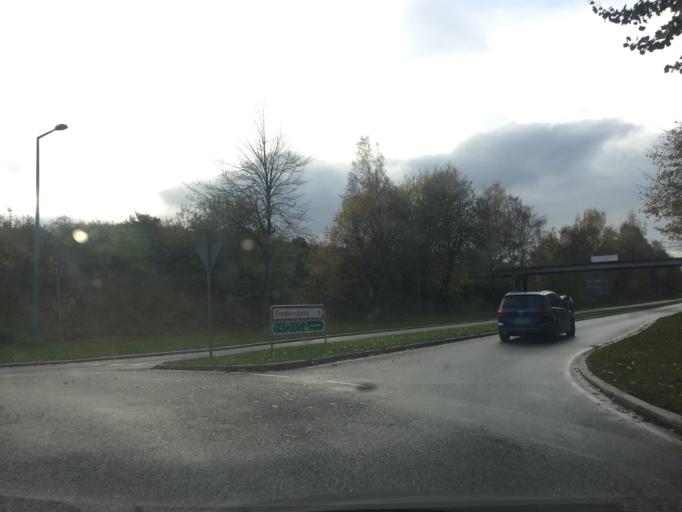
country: DK
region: Capital Region
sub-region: Fredensborg Kommune
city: Humlebaek
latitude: 55.9647
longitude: 12.5259
